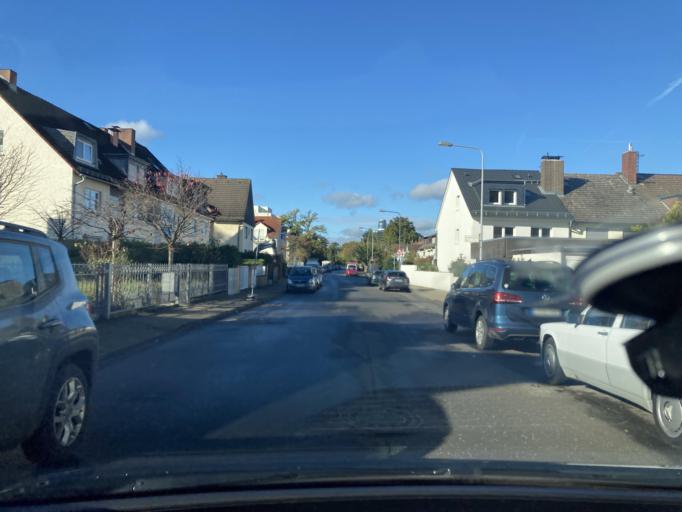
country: DE
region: Hesse
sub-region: Regierungsbezirk Darmstadt
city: Frankfurt am Main
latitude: 50.0962
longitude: 8.7166
